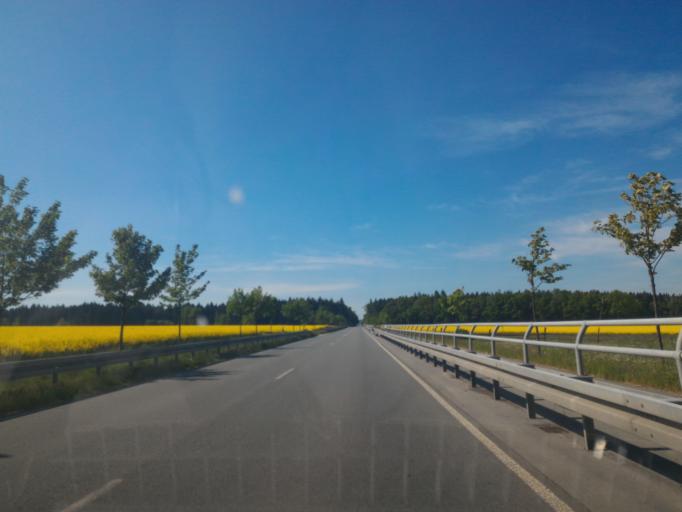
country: DE
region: Saxony
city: Durrhennersdorf
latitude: 51.0224
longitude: 14.6244
